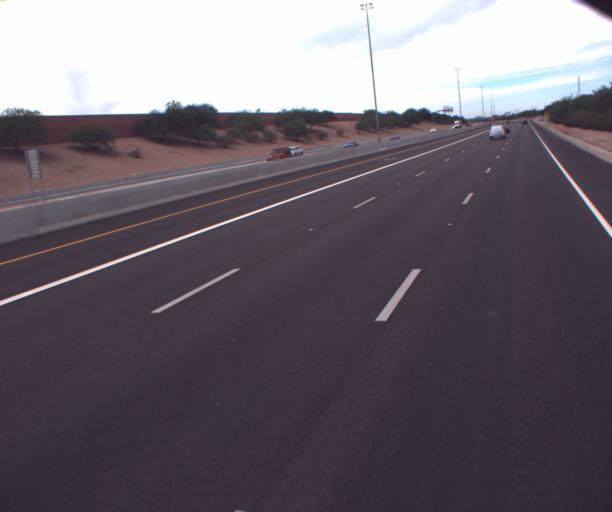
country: US
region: Arizona
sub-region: Maricopa County
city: Mesa
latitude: 33.4656
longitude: -111.7925
